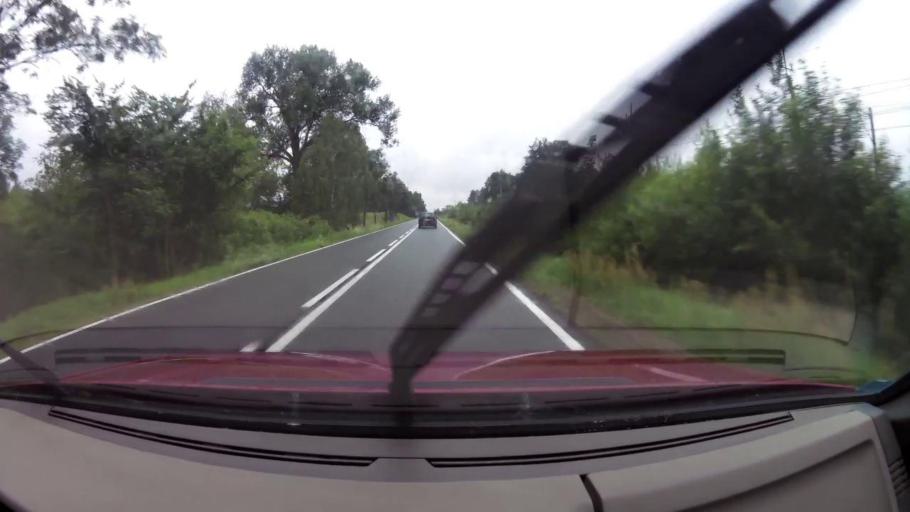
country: PL
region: West Pomeranian Voivodeship
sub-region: Powiat stargardzki
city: Chociwel
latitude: 53.4452
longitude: 15.3084
